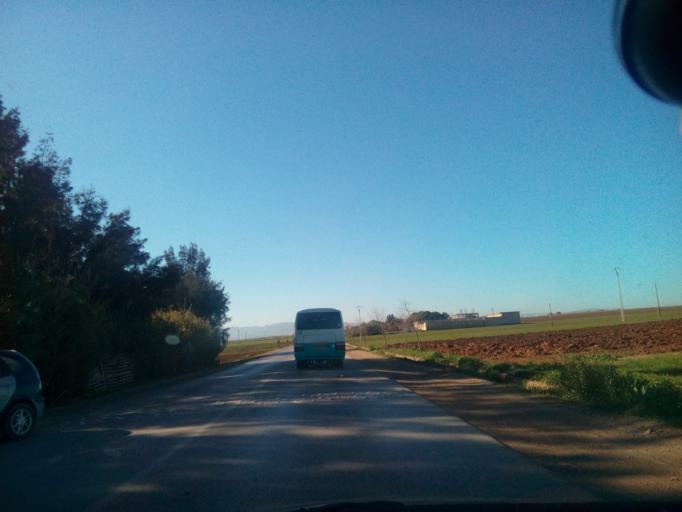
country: DZ
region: Relizane
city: Djidiouia
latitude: 35.8947
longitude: 0.6642
